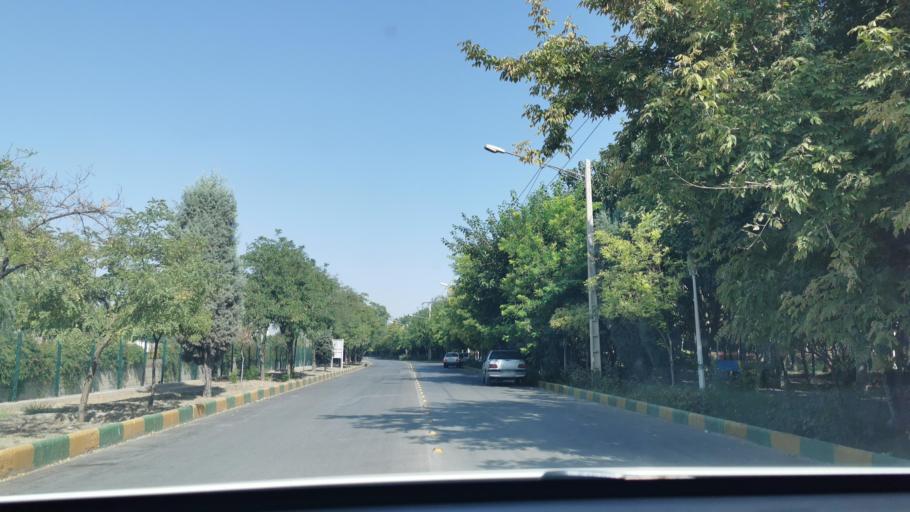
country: IR
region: Razavi Khorasan
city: Mashhad
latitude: 36.3288
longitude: 59.6373
